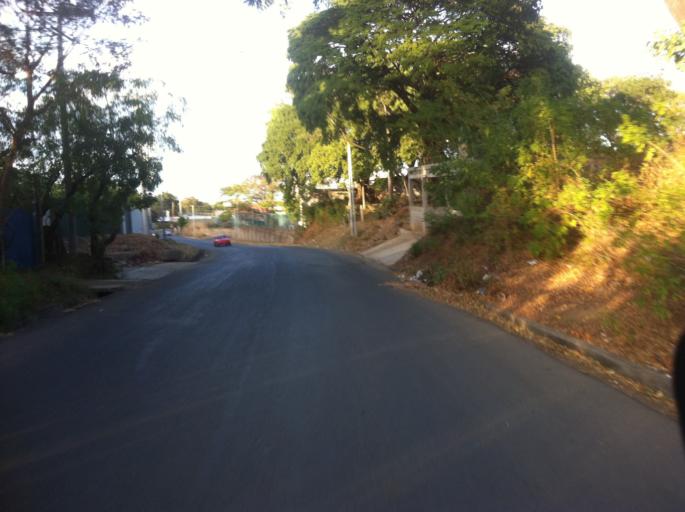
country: NI
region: Managua
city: Managua
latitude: 12.1053
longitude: -86.3006
